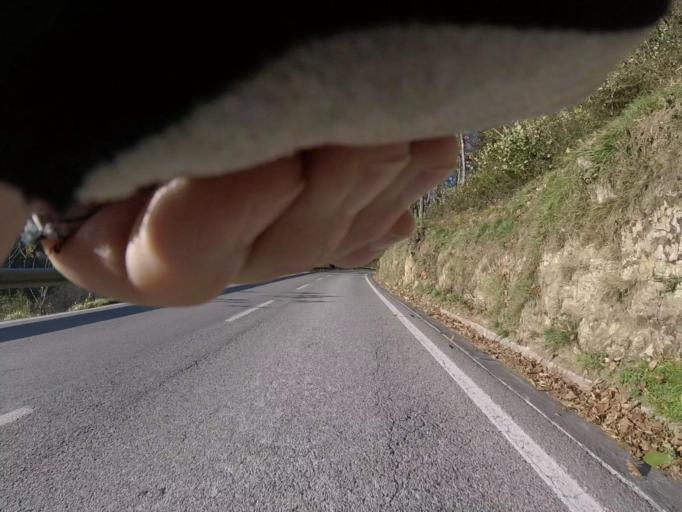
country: ES
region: Navarre
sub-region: Provincia de Navarra
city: Igantzi
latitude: 43.2269
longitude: -1.6842
